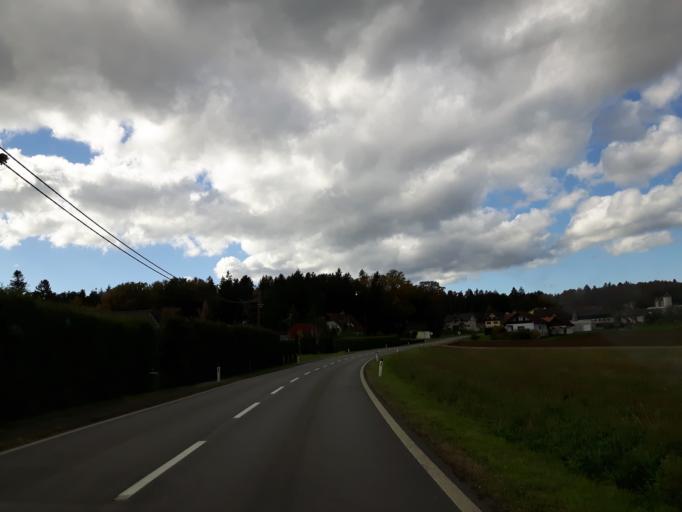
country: AT
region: Styria
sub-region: Politischer Bezirk Leibnitz
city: Breitenfeld am Tannenriegel
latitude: 46.8419
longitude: 15.6354
